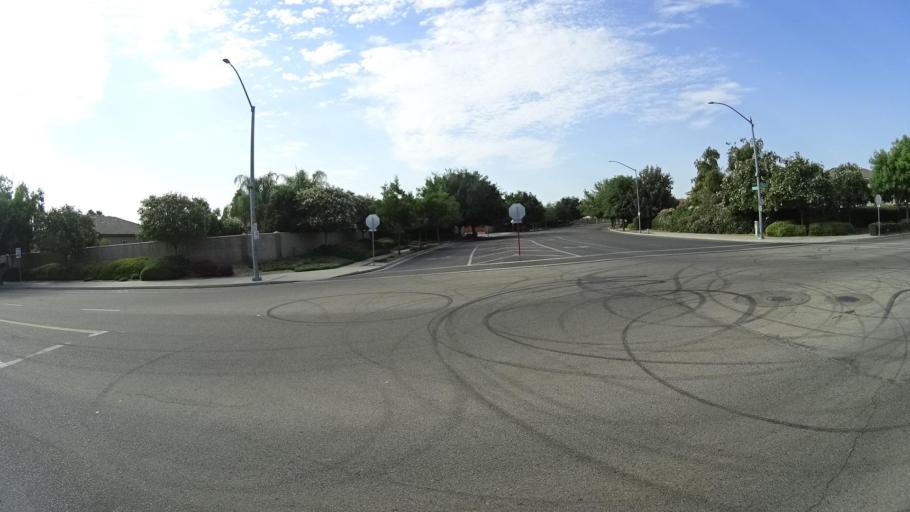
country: US
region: California
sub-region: Fresno County
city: Sunnyside
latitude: 36.7203
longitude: -119.6915
